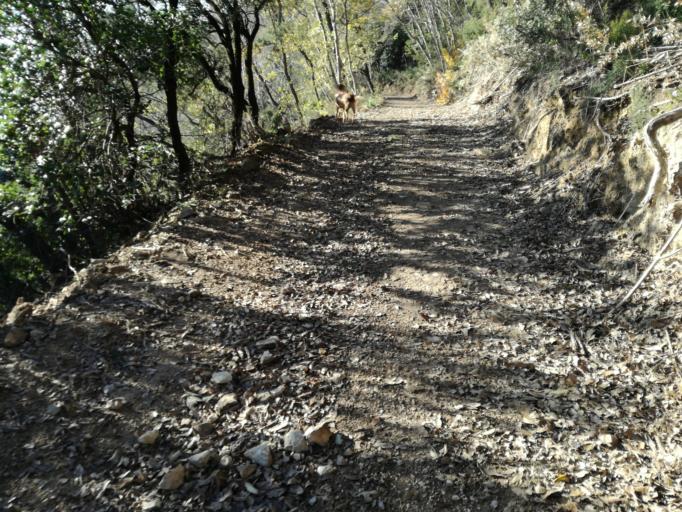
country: IT
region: Veneto
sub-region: Provincia di Padova
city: Arqua Petrarca
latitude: 45.2790
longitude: 11.7327
